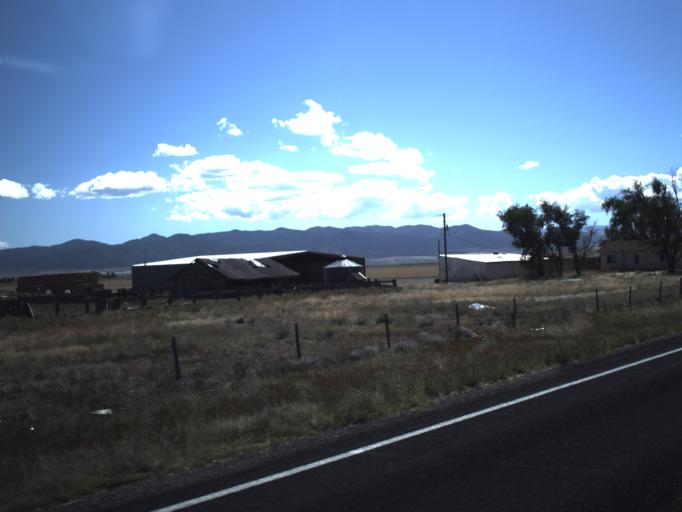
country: US
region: Utah
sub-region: Washington County
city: Enterprise
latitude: 37.6796
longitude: -113.6565
